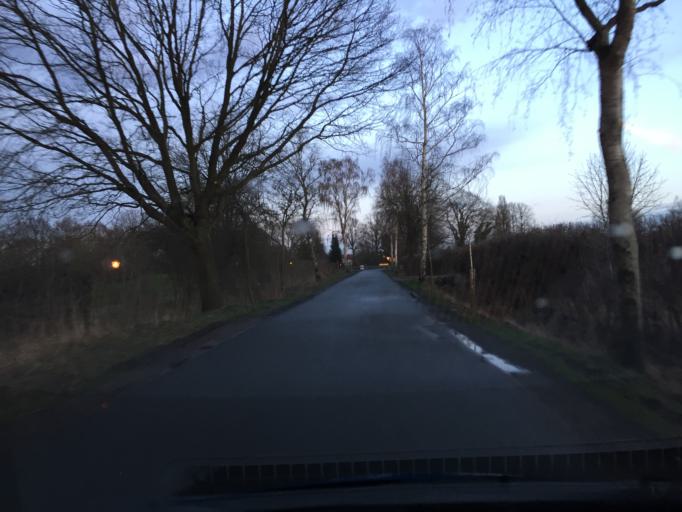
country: DE
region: Lower Saxony
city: Ludersburg
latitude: 53.3238
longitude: 10.5744
